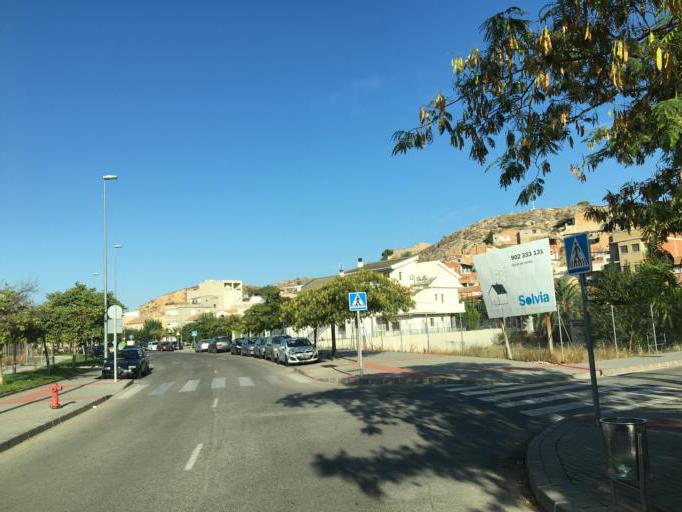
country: ES
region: Murcia
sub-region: Murcia
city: Murcia
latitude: 38.0165
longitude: -1.1471
